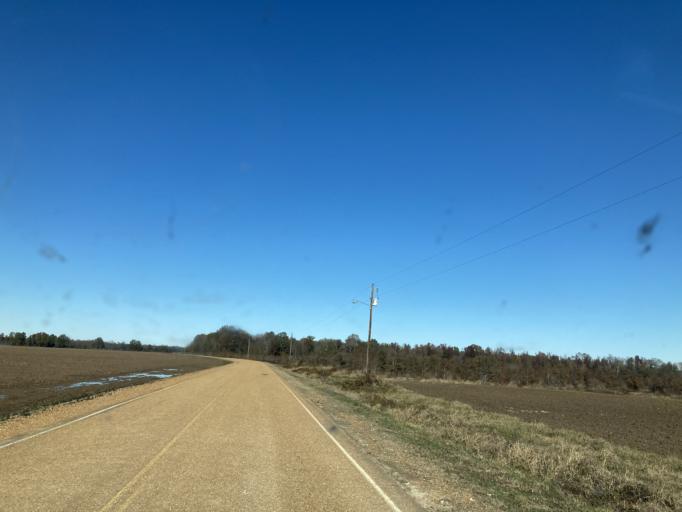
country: US
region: Mississippi
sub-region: Yazoo County
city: Yazoo City
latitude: 32.7430
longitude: -90.6343
